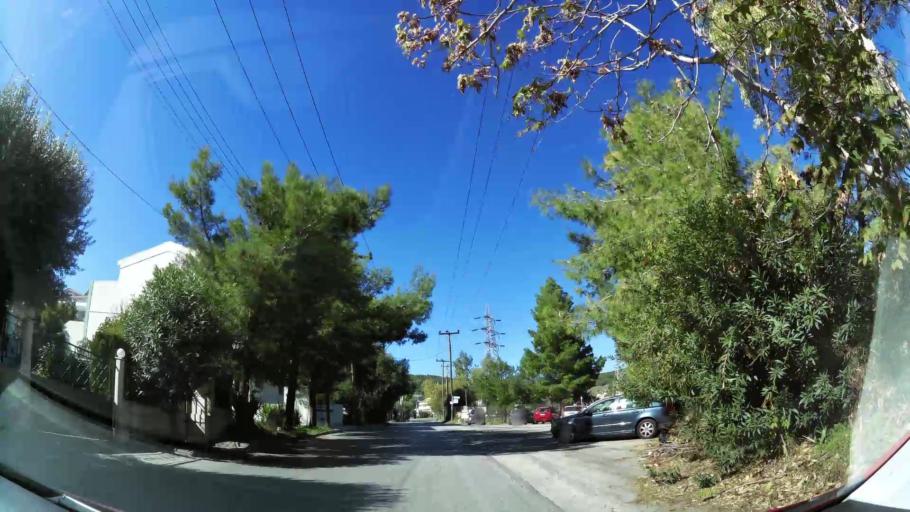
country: GR
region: Attica
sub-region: Nomarchia Anatolikis Attikis
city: Leondarion
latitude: 37.9920
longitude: 23.8508
